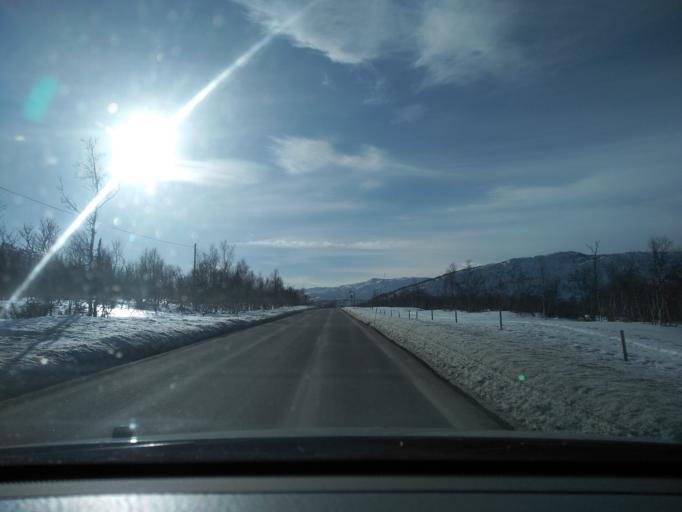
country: NO
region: Aust-Agder
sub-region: Bykle
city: Hovden
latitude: 59.6471
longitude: 7.4664
